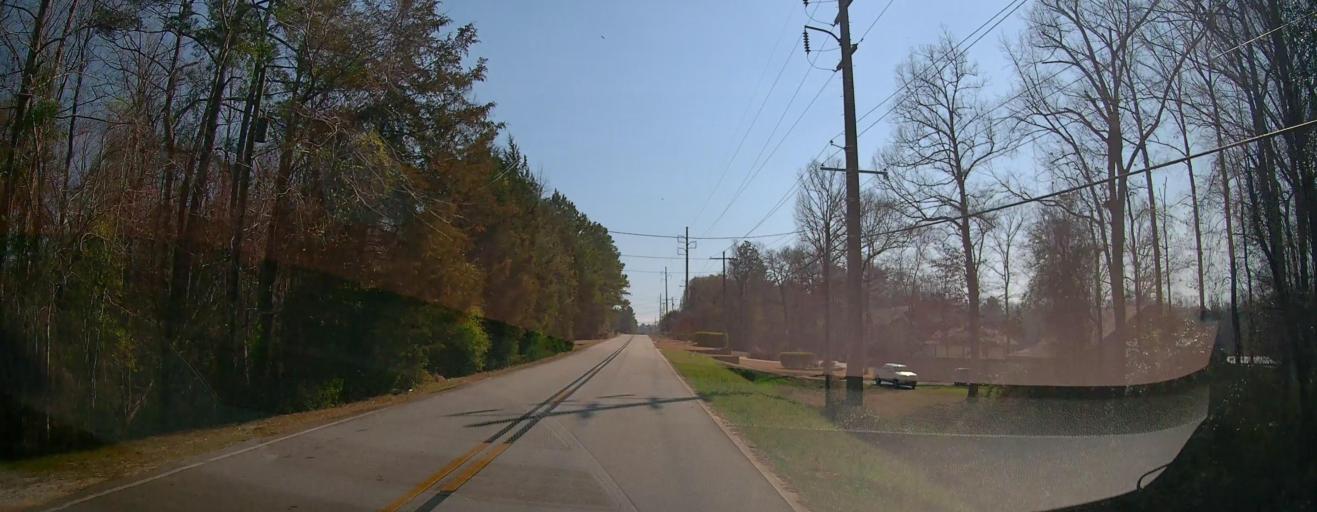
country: US
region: Georgia
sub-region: Houston County
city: Perry
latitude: 32.4697
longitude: -83.7589
